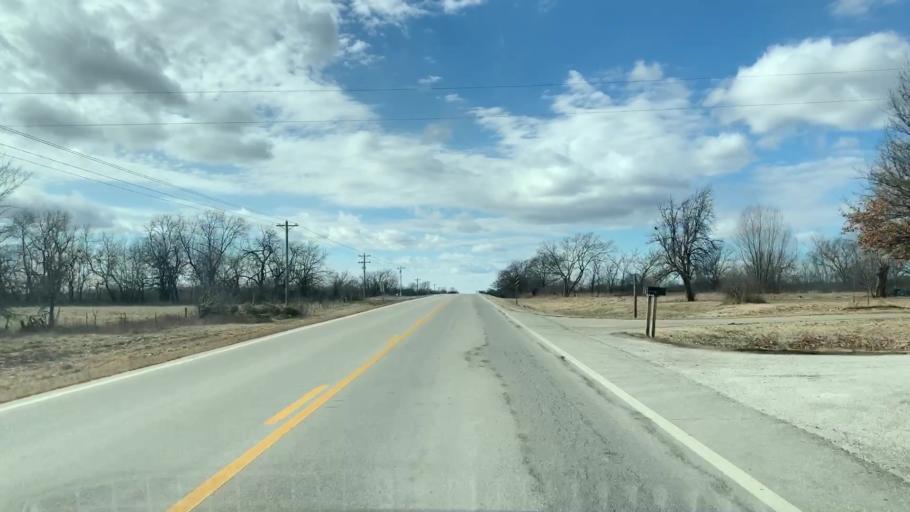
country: US
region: Kansas
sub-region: Neosho County
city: Erie
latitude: 37.5292
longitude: -95.2781
